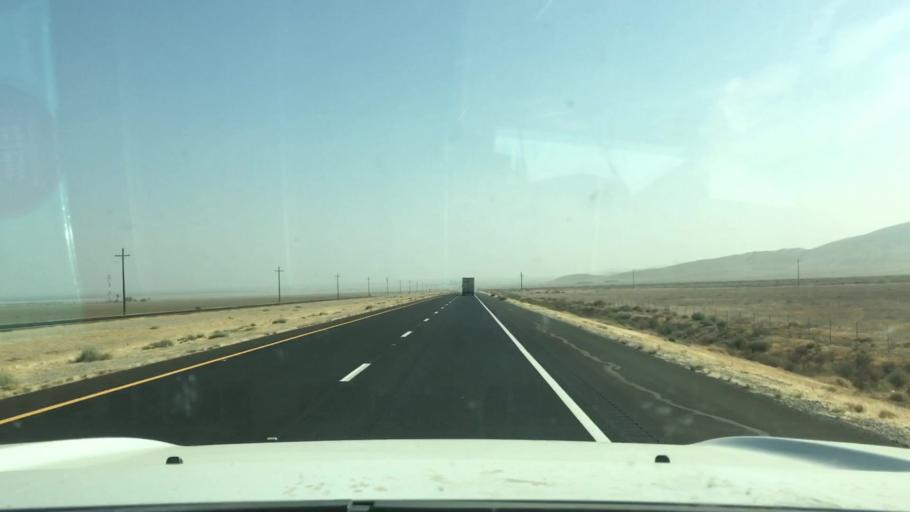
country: US
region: California
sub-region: San Luis Obispo County
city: Shandon
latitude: 35.6611
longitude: -120.0616
